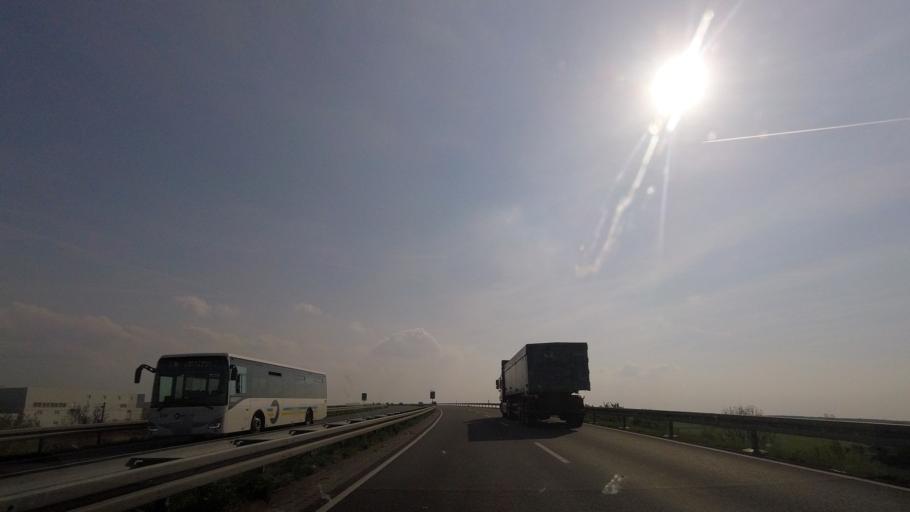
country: DE
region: Saxony-Anhalt
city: Wittenburg
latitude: 51.8408
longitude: 12.6290
